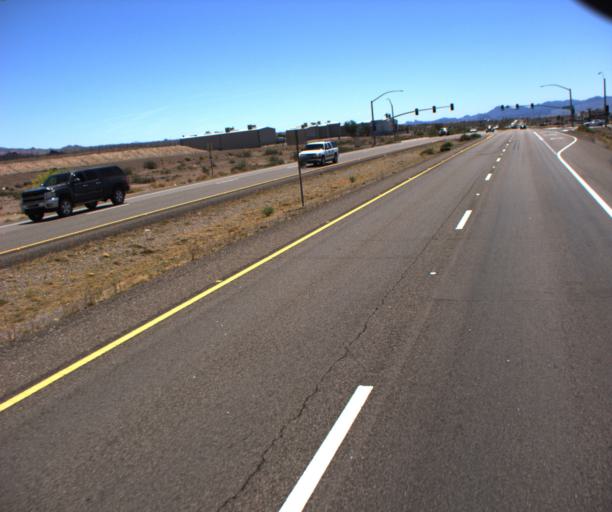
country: US
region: Arizona
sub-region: Mohave County
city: Desert Hills
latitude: 34.5744
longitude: -114.3653
